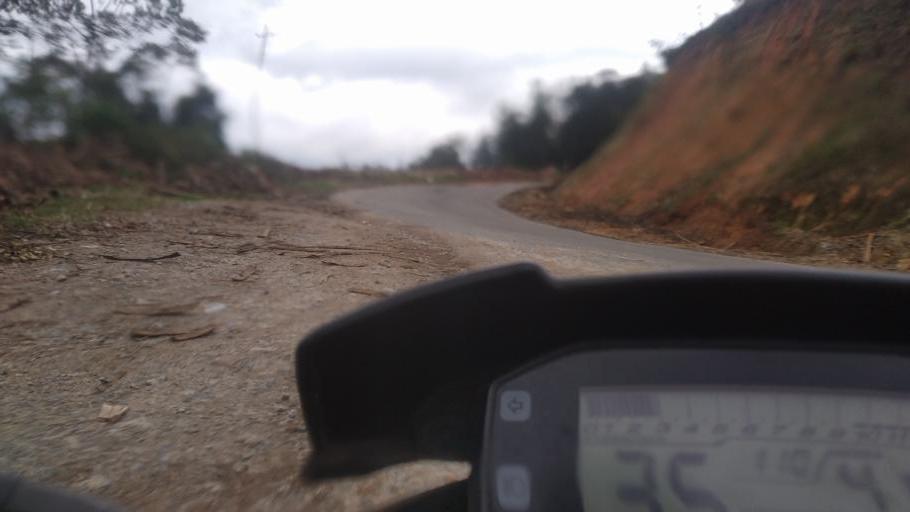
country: IN
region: Kerala
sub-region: Idukki
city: Munnar
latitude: 10.0835
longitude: 77.0696
